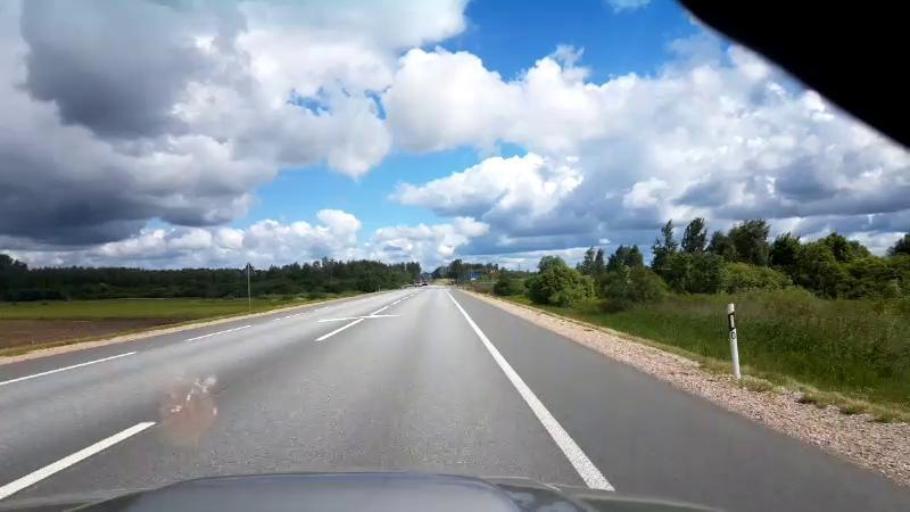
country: LV
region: Lecava
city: Iecava
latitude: 56.6236
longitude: 24.2198
